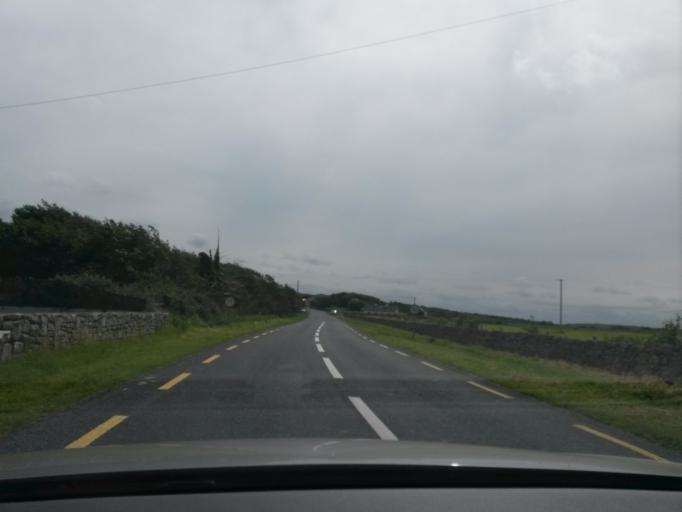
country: IE
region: Connaught
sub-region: Sligo
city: Sligo
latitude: 54.4357
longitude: -8.4561
